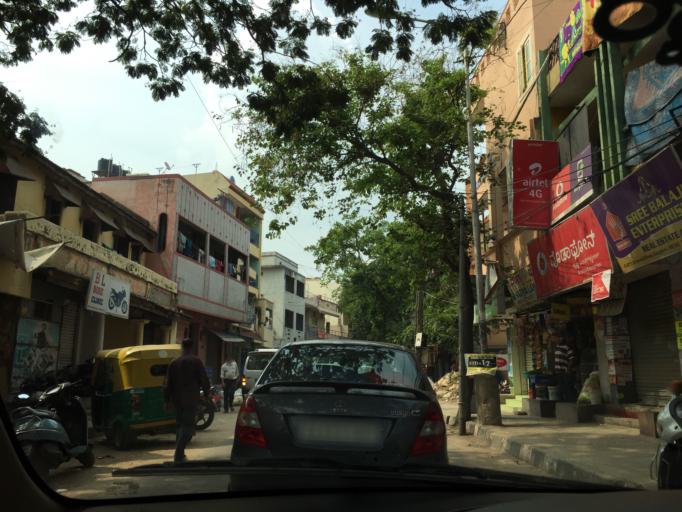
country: IN
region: Karnataka
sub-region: Bangalore Urban
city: Bangalore
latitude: 12.9854
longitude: 77.6118
